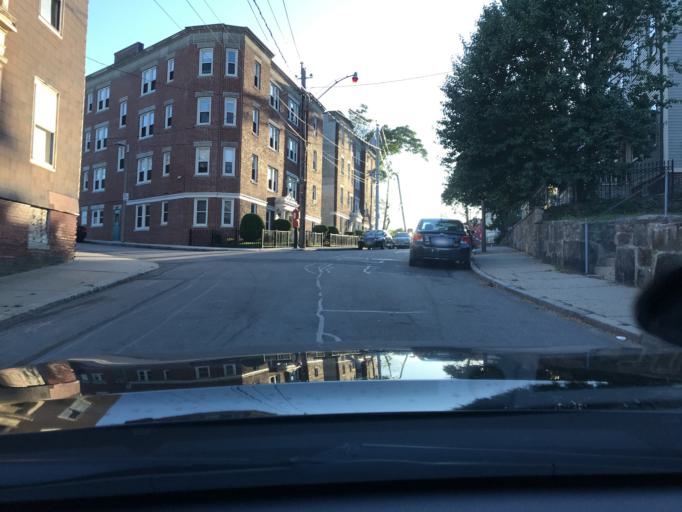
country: US
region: Massachusetts
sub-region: Suffolk County
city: South Boston
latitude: 42.3253
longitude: -71.0846
